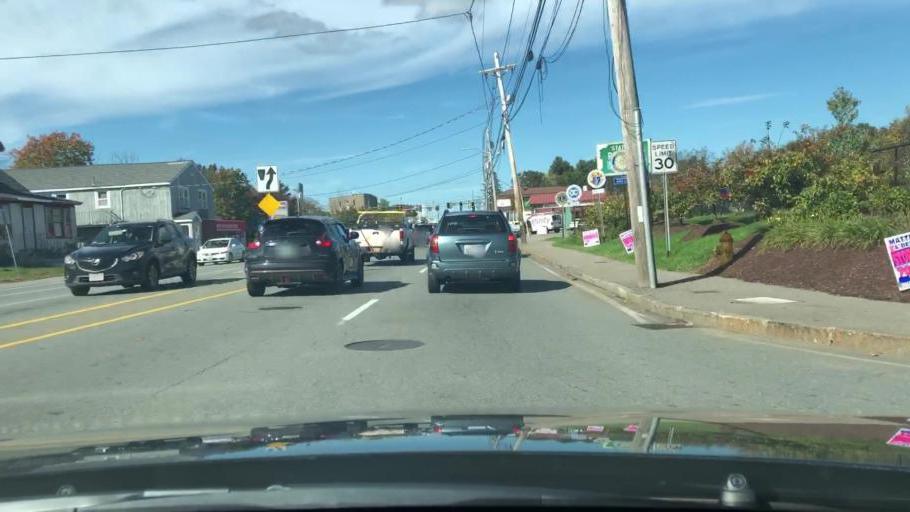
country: US
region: Massachusetts
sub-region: Essex County
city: Methuen
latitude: 42.7411
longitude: -71.1977
